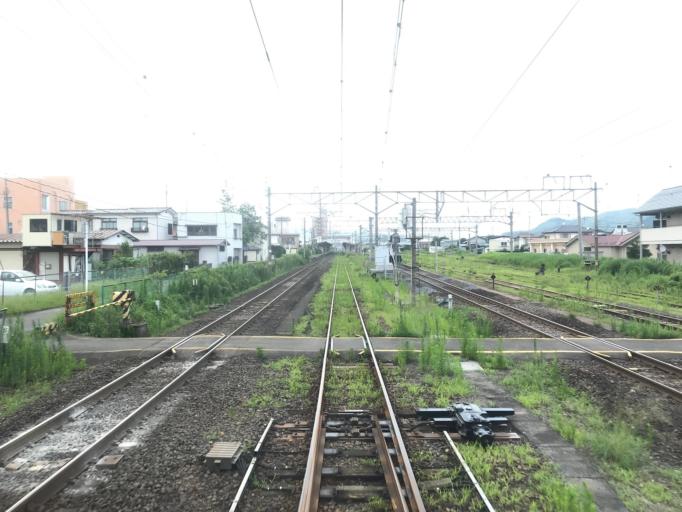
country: JP
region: Miyagi
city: Shiroishi
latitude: 38.0005
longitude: 140.6258
